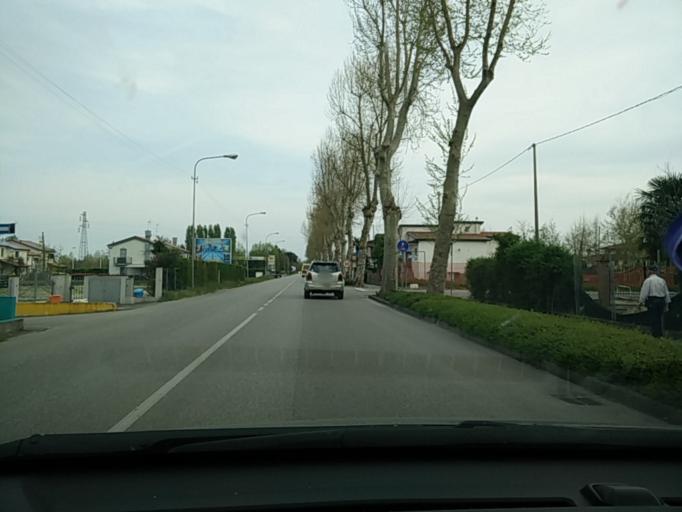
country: IT
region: Veneto
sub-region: Provincia di Venezia
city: Noventa di Piave
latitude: 45.6513
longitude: 12.5417
